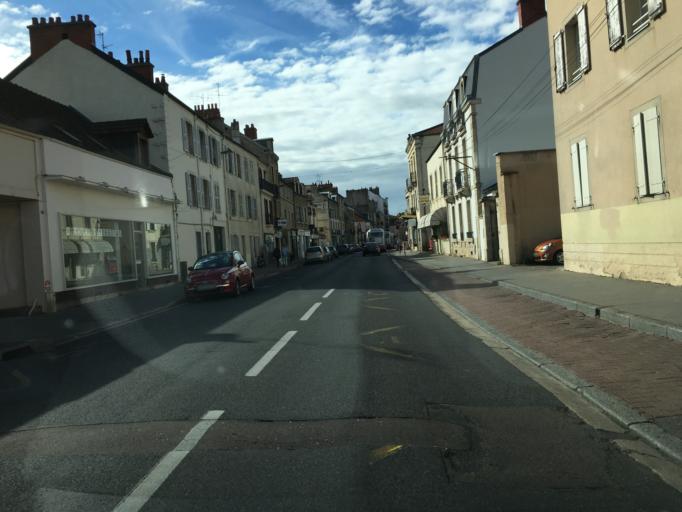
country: FR
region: Bourgogne
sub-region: Departement de la Cote-d'Or
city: Longvic
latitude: 47.3142
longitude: 5.0483
